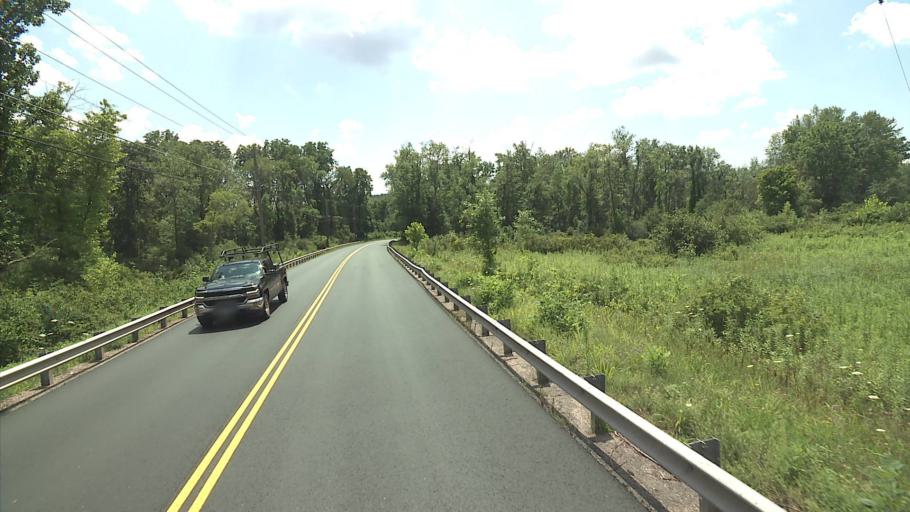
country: US
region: Connecticut
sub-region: Litchfield County
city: Canaan
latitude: 41.9707
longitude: -73.3585
